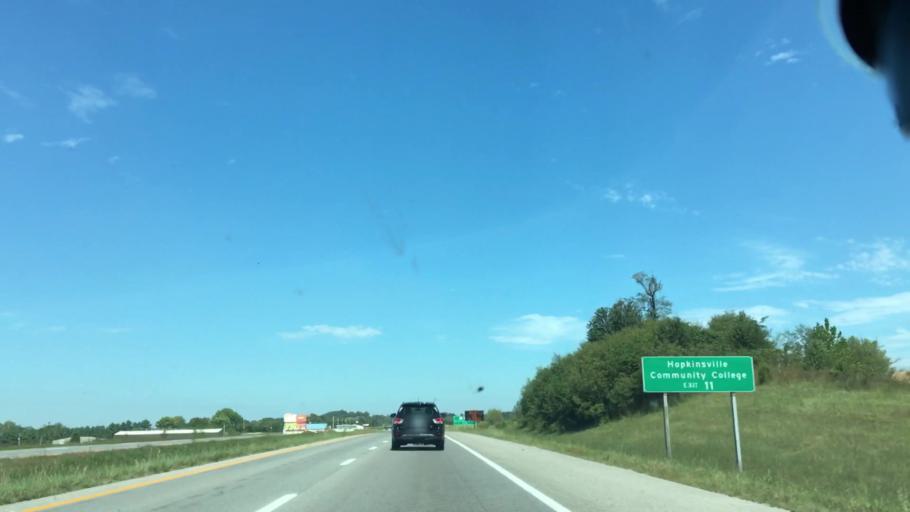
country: US
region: Kentucky
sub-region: Christian County
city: Hopkinsville
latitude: 36.8847
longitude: -87.4687
